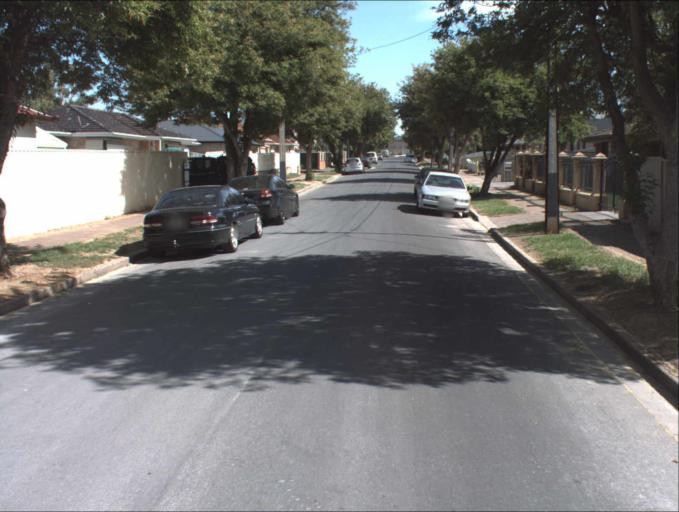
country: AU
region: South Australia
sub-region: Port Adelaide Enfield
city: Klemzig
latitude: -34.8774
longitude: 138.6399
